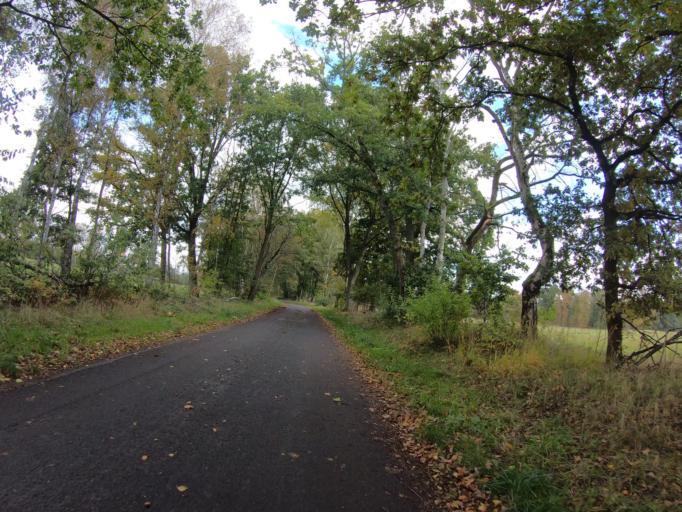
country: DE
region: Lower Saxony
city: Wagenhoff
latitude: 52.5474
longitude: 10.5543
